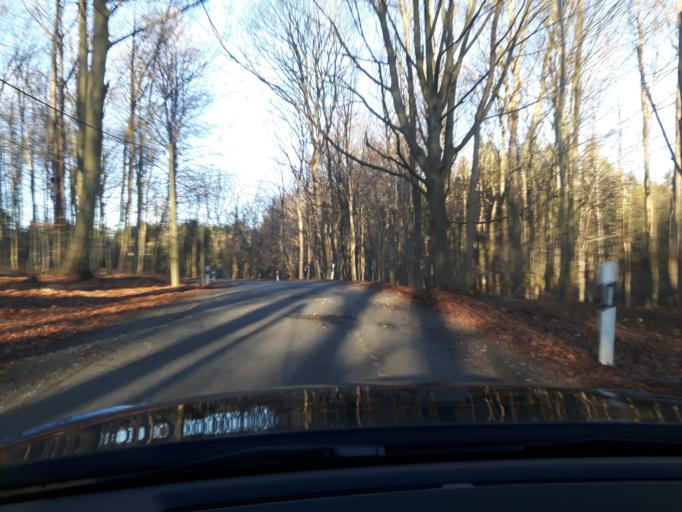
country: DE
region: Mecklenburg-Vorpommern
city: Putbus
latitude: 54.3624
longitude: 13.4382
